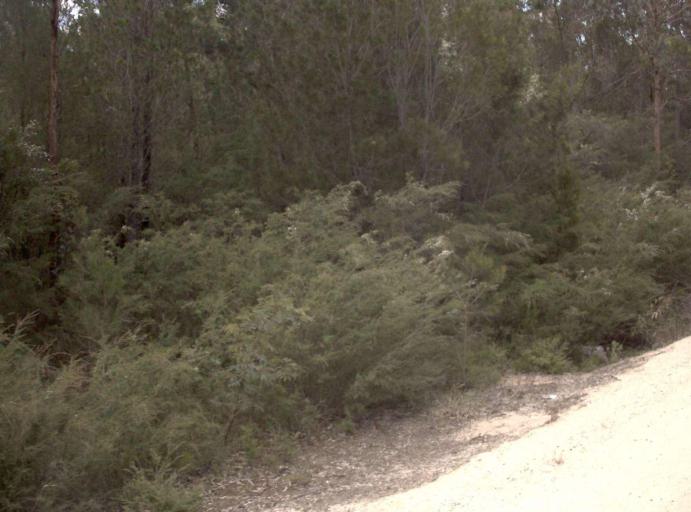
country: AU
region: New South Wales
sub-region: Bega Valley
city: Eden
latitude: -37.4247
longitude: 149.6458
